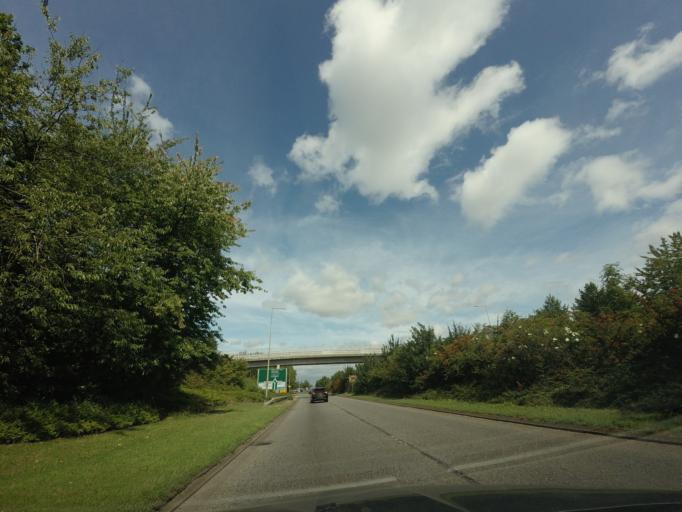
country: GB
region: England
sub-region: Milton Keynes
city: Simpson
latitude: 52.0238
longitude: -0.6890
